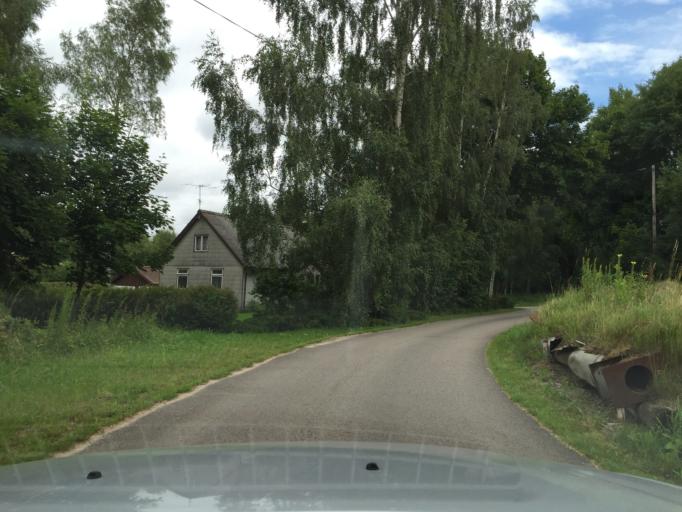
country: SE
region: Skane
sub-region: Hassleholms Kommun
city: Sosdala
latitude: 56.0385
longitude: 13.6893
